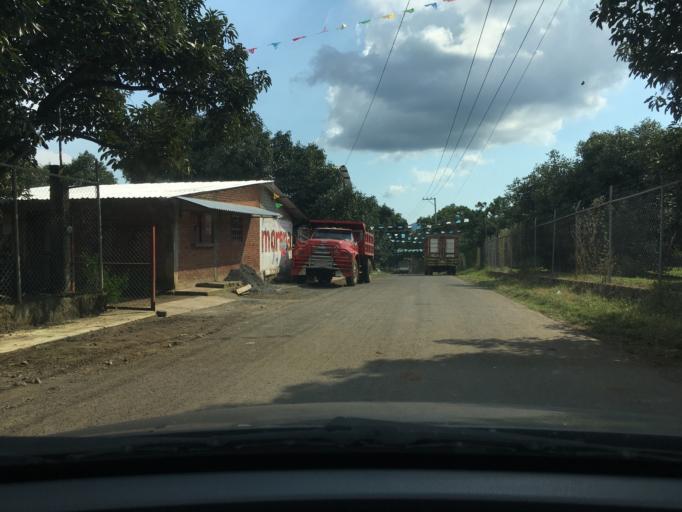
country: MX
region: Michoacan
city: Tingambato
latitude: 19.4516
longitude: -101.8673
